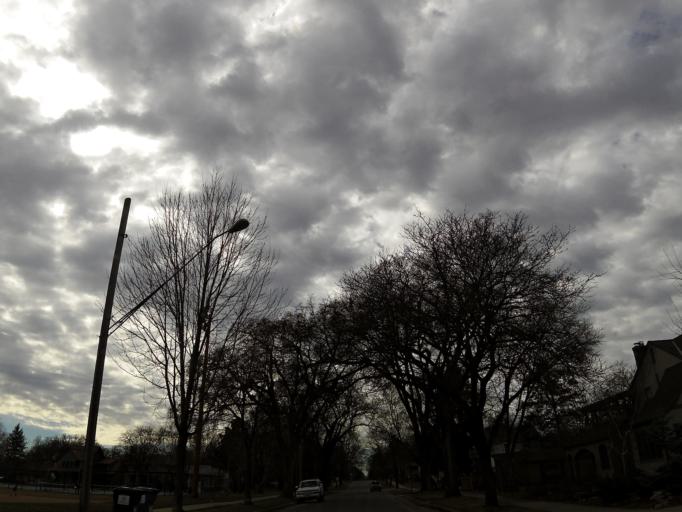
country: US
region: Minnesota
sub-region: Hennepin County
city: Saint Louis Park
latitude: 44.9270
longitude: -93.3199
